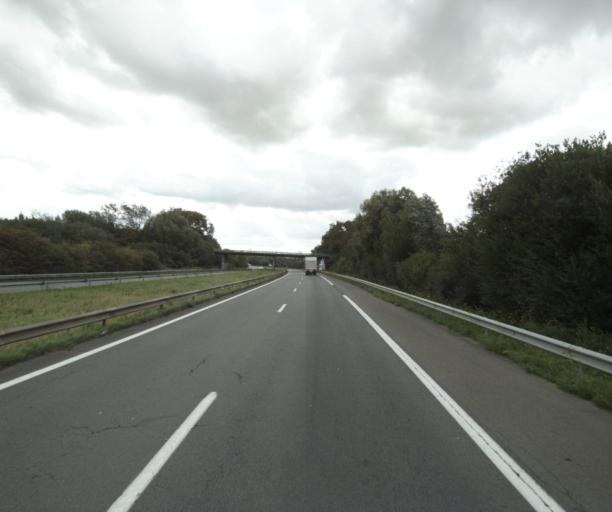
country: FR
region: Nord-Pas-de-Calais
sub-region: Departement du Nord
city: Genech
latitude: 50.5287
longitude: 3.1990
